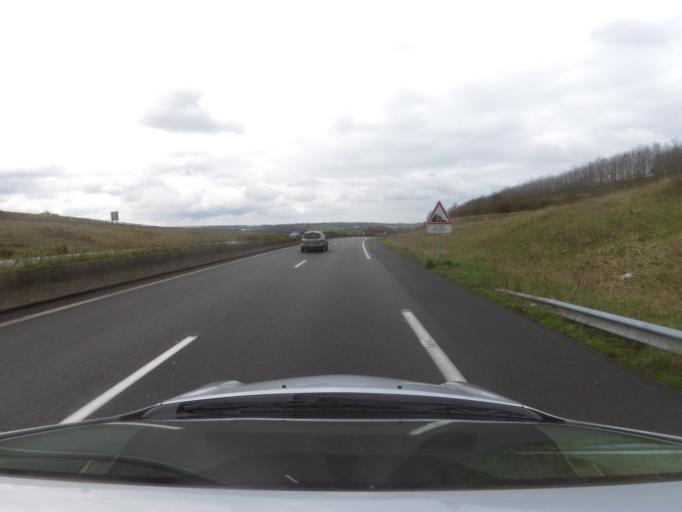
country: FR
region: Nord-Pas-de-Calais
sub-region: Departement du Pas-de-Calais
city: Wimille
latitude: 50.7706
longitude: 1.6486
